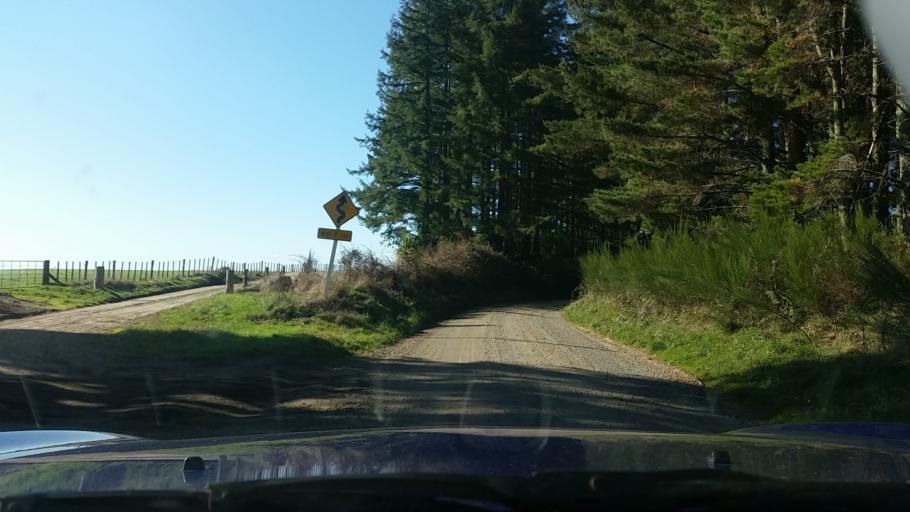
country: NZ
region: Bay of Plenty
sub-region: Whakatane District
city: Murupara
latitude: -38.3463
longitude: 176.5365
